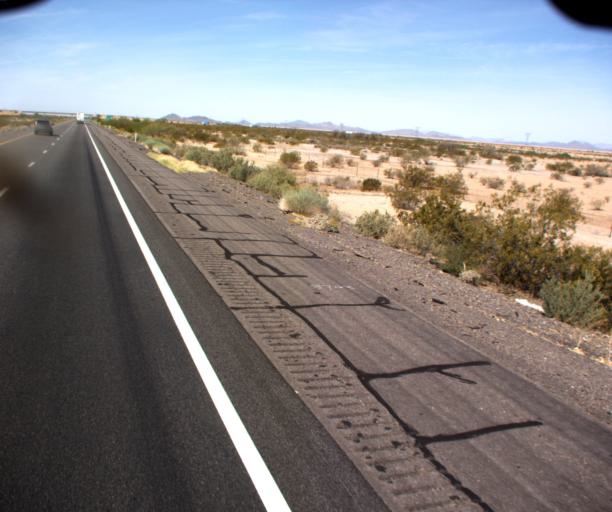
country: US
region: Arizona
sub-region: La Paz County
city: Salome
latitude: 33.5677
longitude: -113.3422
